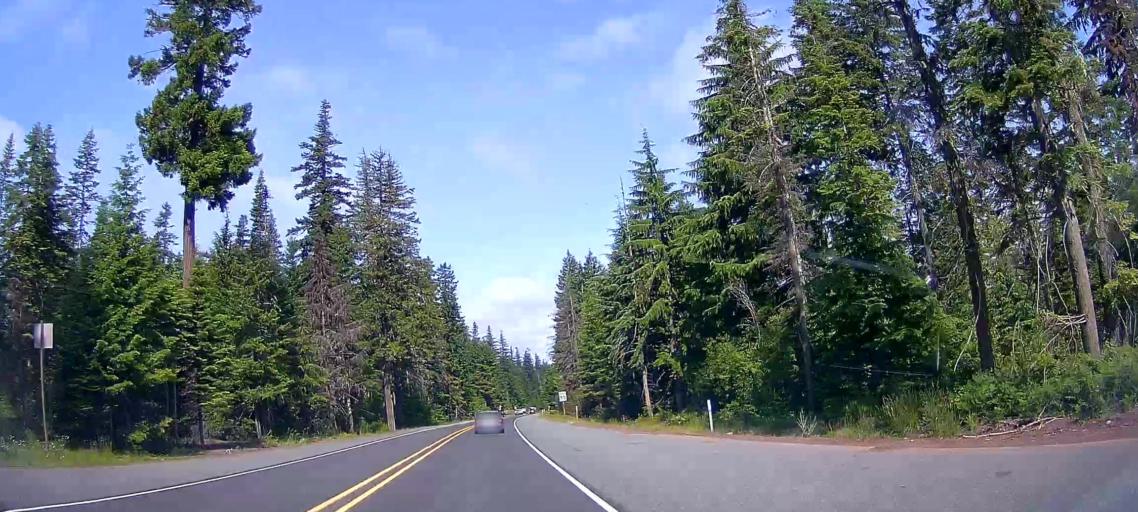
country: US
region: Oregon
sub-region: Clackamas County
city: Mount Hood Village
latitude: 45.1325
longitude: -121.6081
